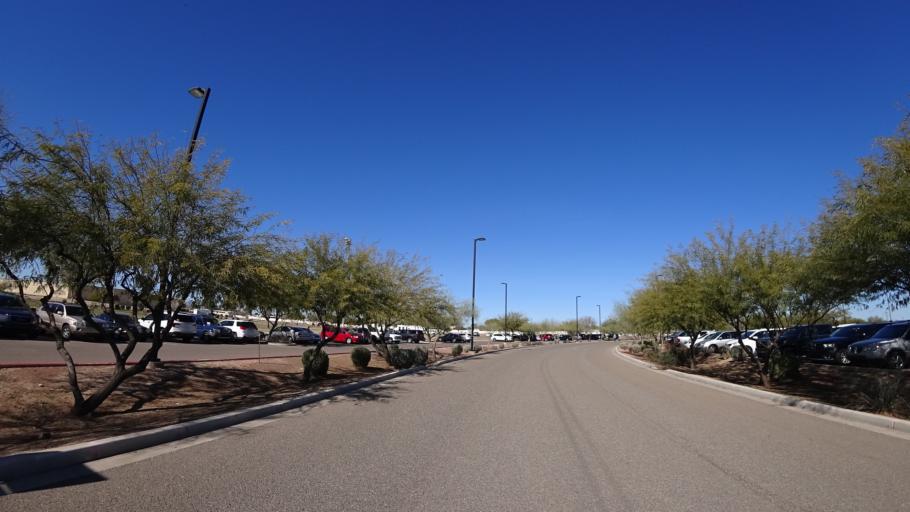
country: US
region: Arizona
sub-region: Maricopa County
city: Avondale
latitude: 33.4190
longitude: -112.3501
